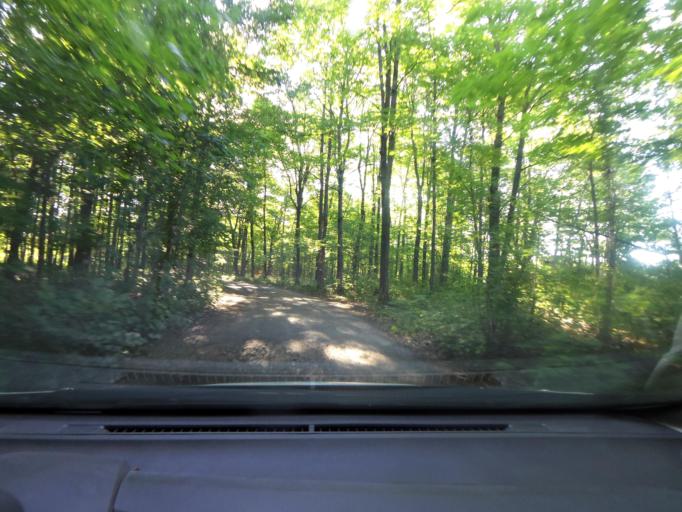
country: CA
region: Quebec
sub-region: Mauricie
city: Becancour
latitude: 46.5447
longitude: -72.3993
